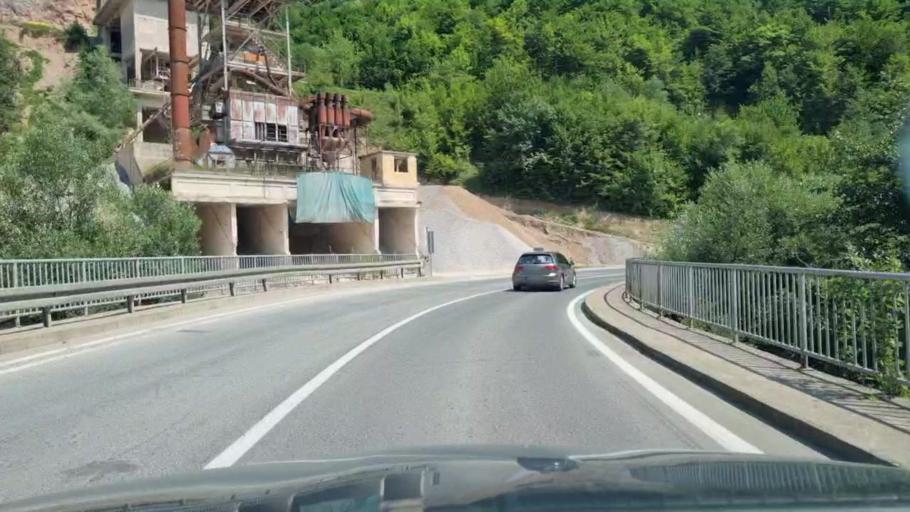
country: BA
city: Stupari
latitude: 44.3364
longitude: 18.6830
